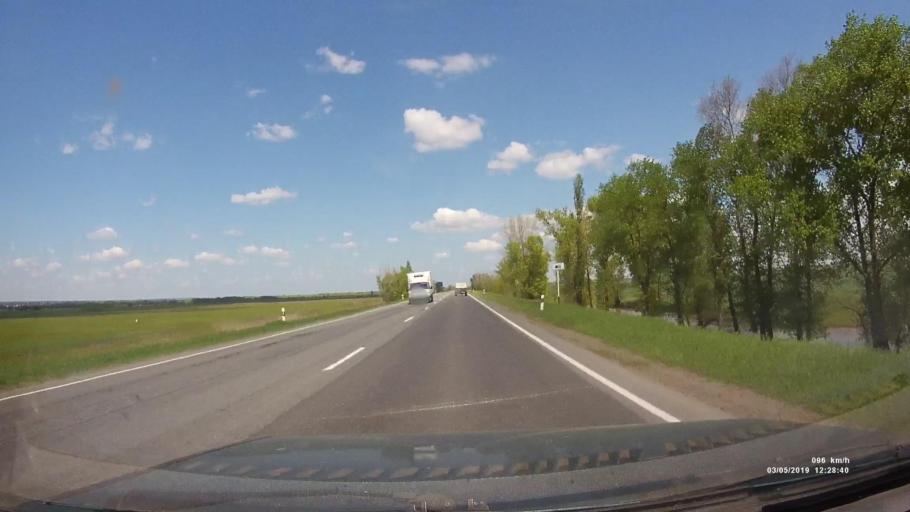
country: RU
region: Rostov
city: Semikarakorsk
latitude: 47.4767
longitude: 40.7303
